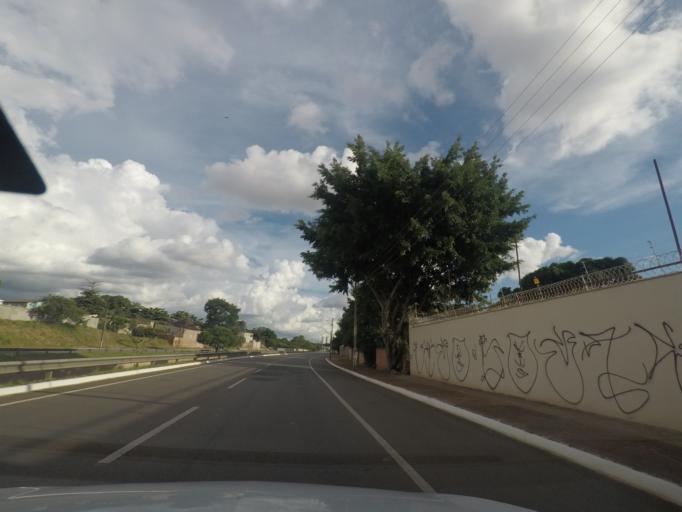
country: BR
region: Goias
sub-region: Goiania
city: Goiania
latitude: -16.6784
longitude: -49.2940
